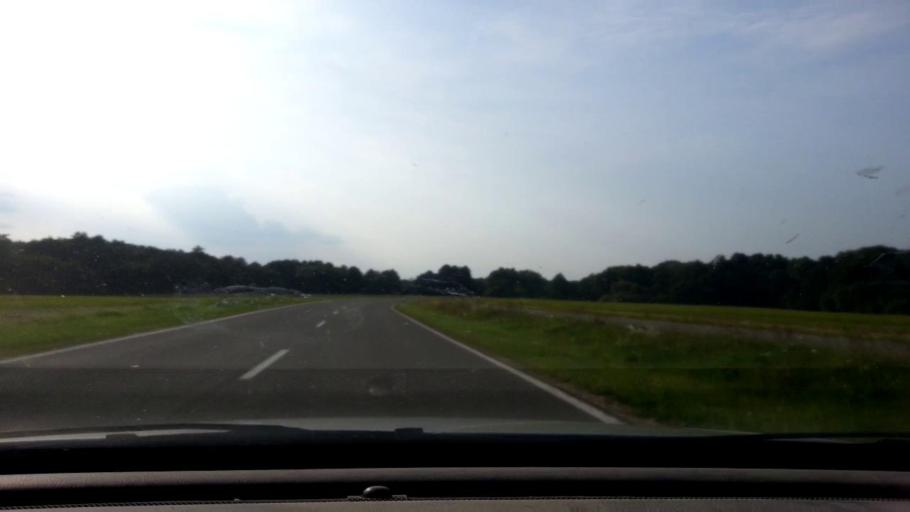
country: DE
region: Bavaria
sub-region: Upper Franconia
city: Memmelsdorf
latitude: 49.9201
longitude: 10.9674
